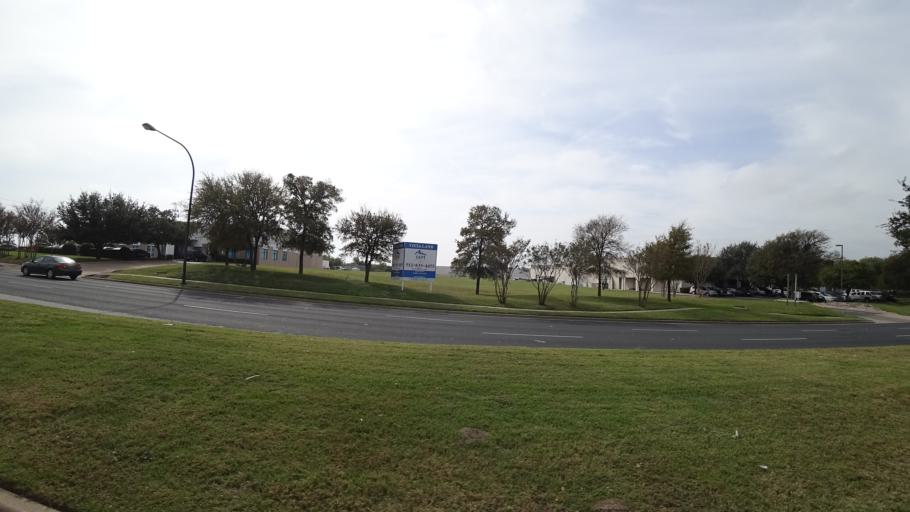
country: US
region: Texas
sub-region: Travis County
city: Wells Branch
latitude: 30.4565
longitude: -97.6702
